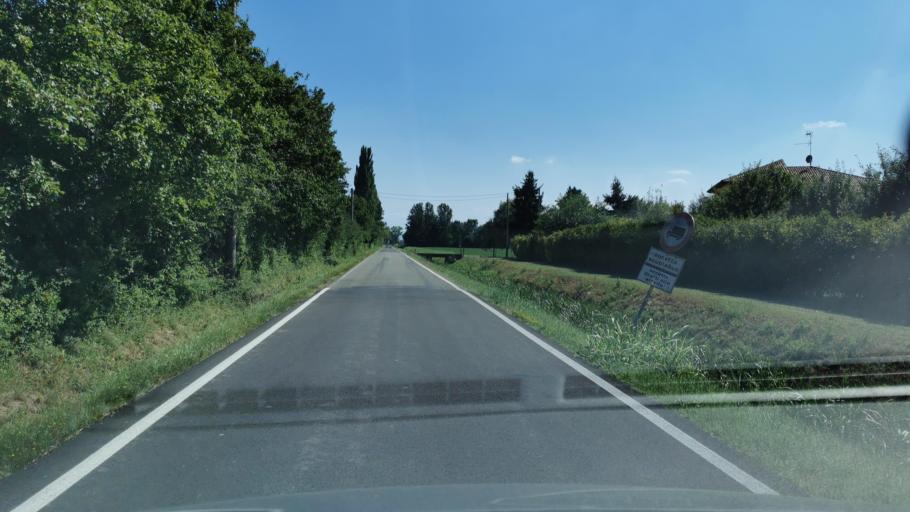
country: IT
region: Emilia-Romagna
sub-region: Provincia di Modena
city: Limidi
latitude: 44.7774
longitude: 10.9181
